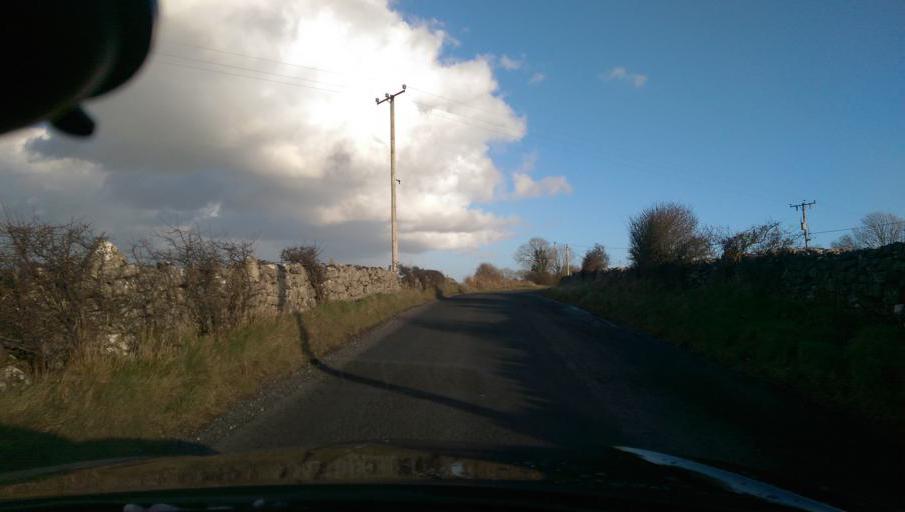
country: IE
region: Connaught
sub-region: County Galway
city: Loughrea
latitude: 53.4177
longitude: -8.5083
